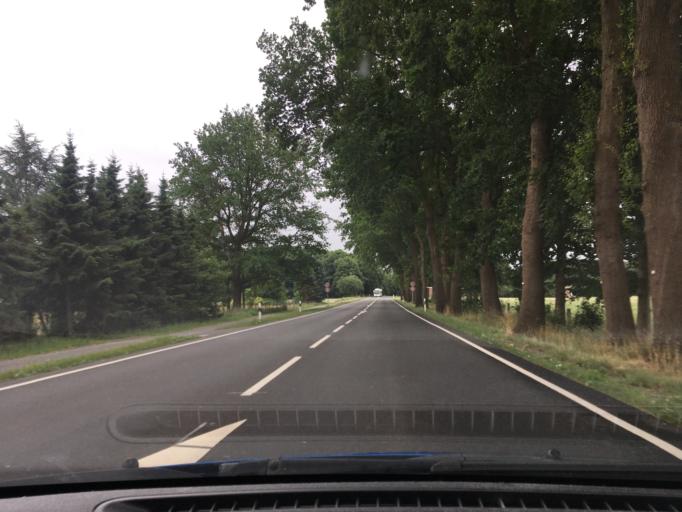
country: DE
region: Lower Saxony
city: Drestedt
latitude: 53.3321
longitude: 9.8128
